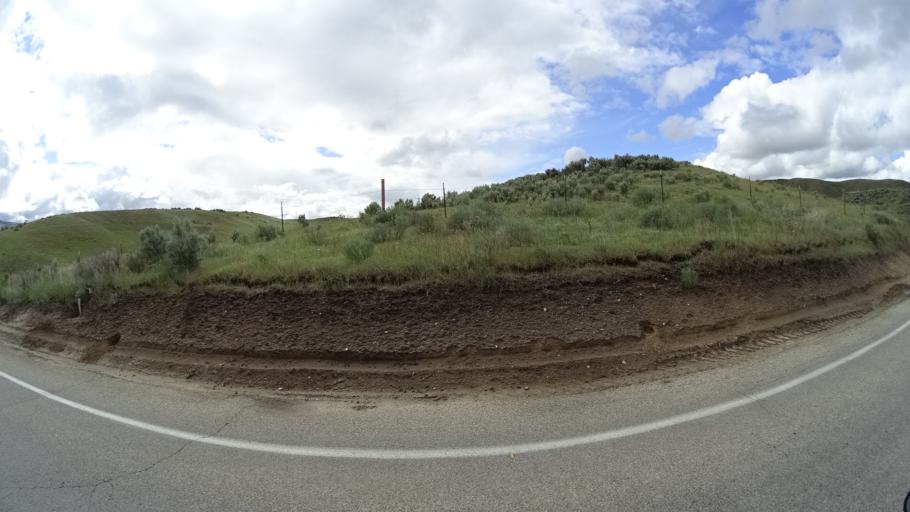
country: US
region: Idaho
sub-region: Ada County
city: Eagle
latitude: 43.7301
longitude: -116.2782
